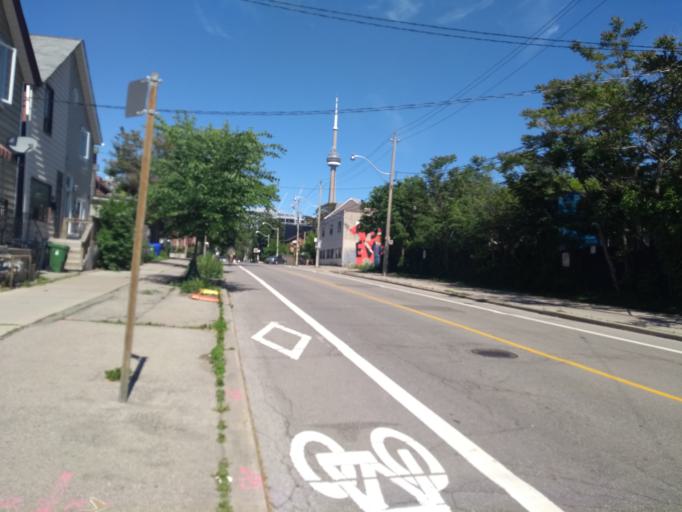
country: CA
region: Ontario
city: Toronto
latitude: 43.6417
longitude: -79.4072
